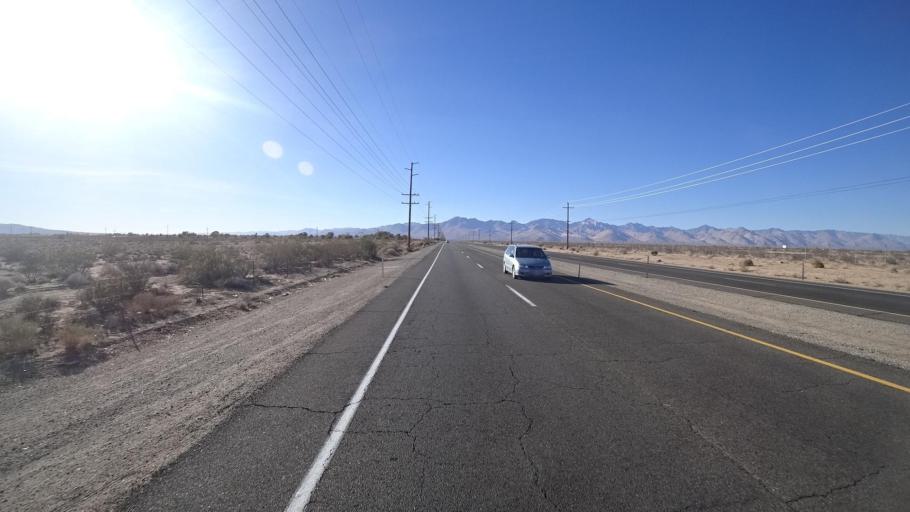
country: US
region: California
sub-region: Kern County
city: China Lake Acres
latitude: 35.6516
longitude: -117.7379
